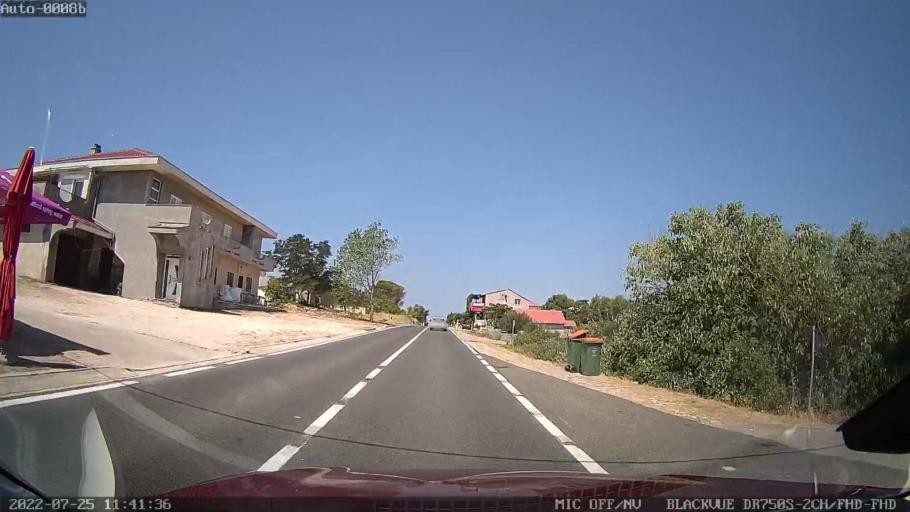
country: HR
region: Zadarska
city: Razanac
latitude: 44.2692
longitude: 15.3456
